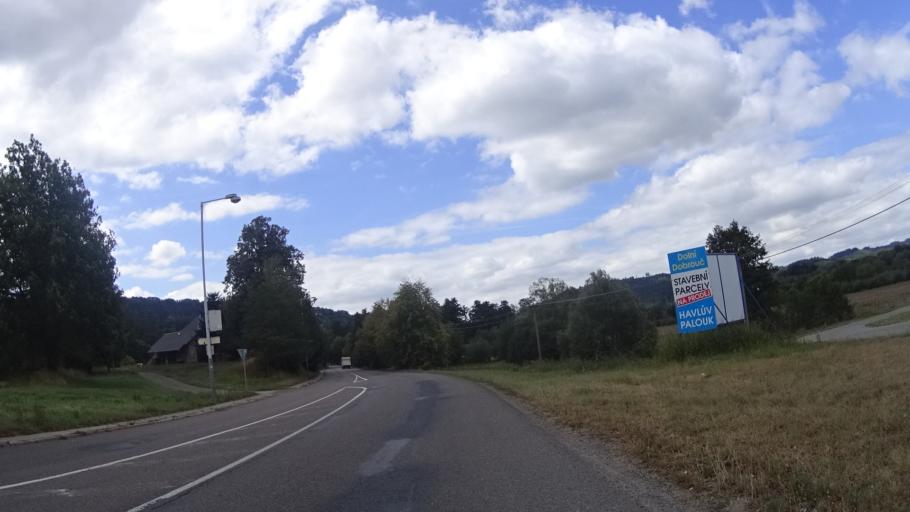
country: CZ
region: Pardubicky
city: Dolni Dobrouc
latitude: 50.0067
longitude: 16.4729
